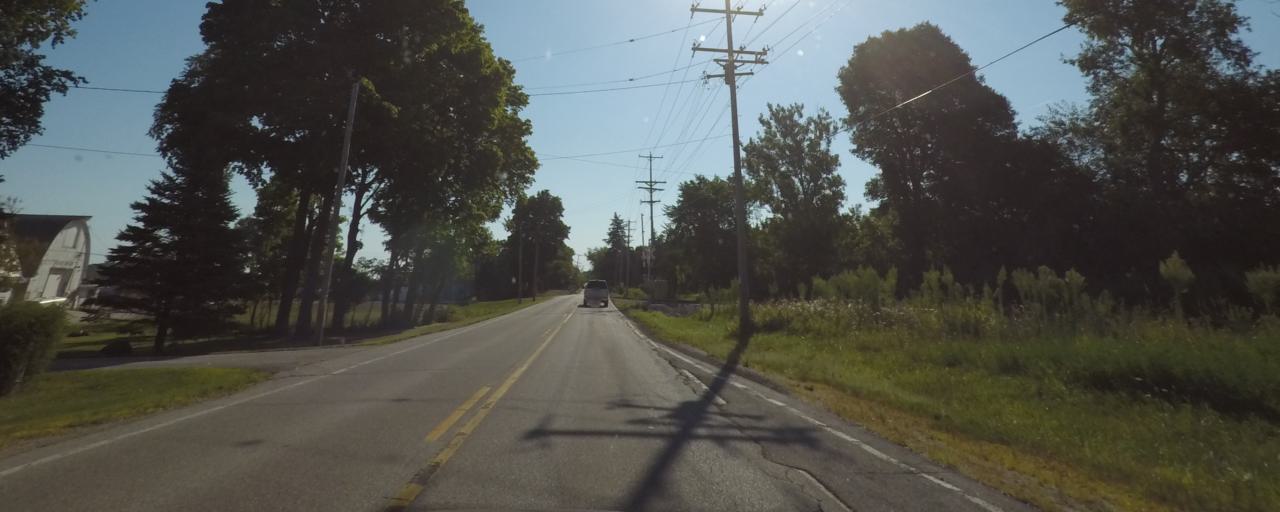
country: US
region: Wisconsin
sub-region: Waukesha County
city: Wales
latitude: 42.9880
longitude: -88.3179
